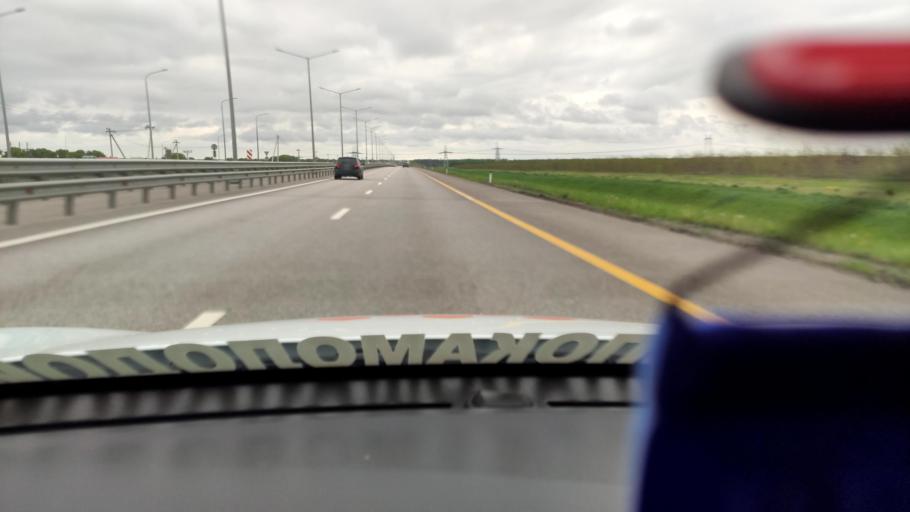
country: RU
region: Voronezj
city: Podkletnoye
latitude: 51.5573
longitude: 39.4849
